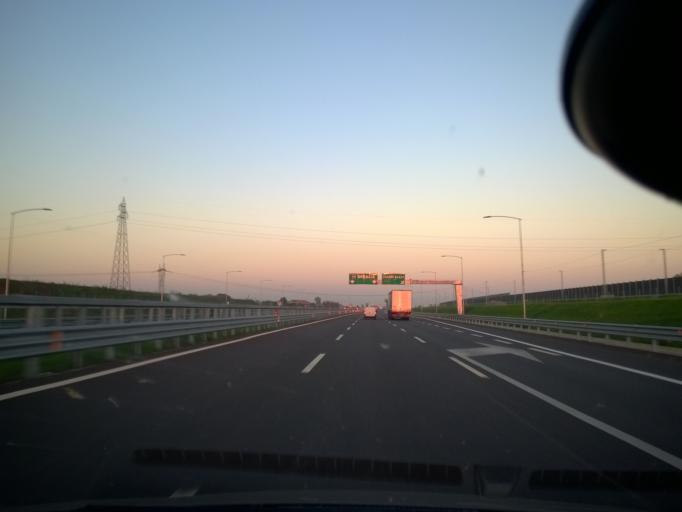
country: IT
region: Lombardy
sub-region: Provincia di Brescia
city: Chiari
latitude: 45.5144
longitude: 9.9152
